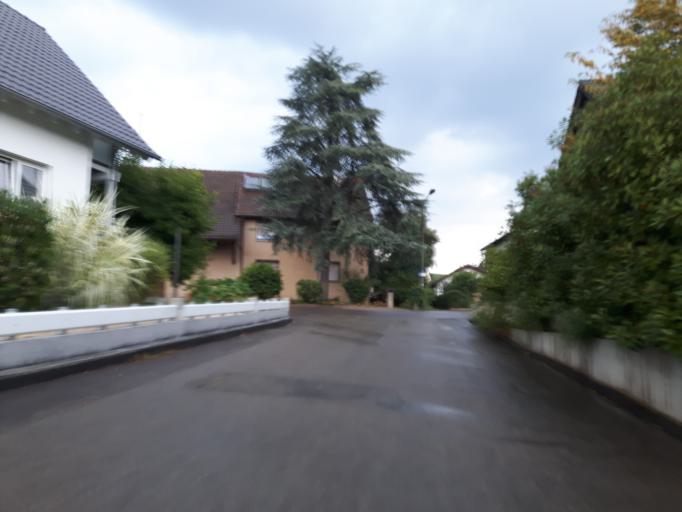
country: DE
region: Baden-Wuerttemberg
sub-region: Regierungsbezirk Stuttgart
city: Eberstadt
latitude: 49.1809
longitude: 9.2987
